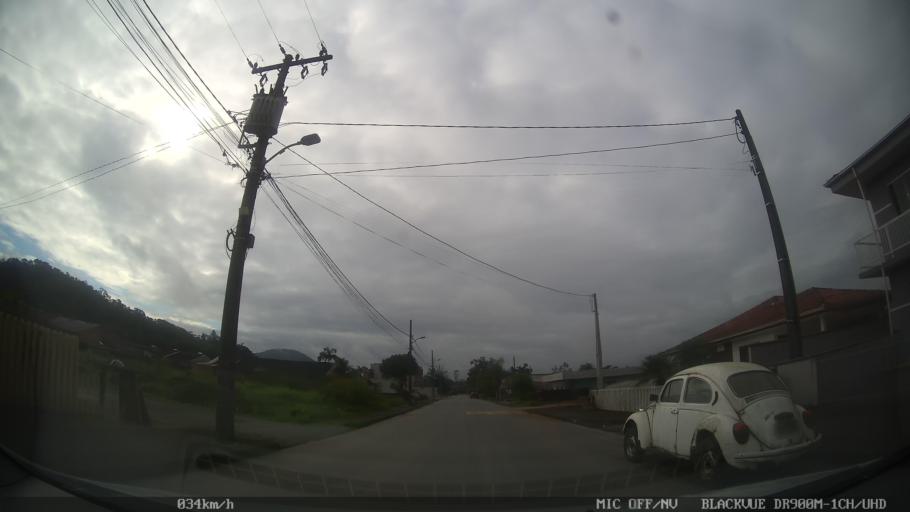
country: BR
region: Santa Catarina
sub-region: Joinville
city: Joinville
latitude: -26.0305
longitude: -48.8480
